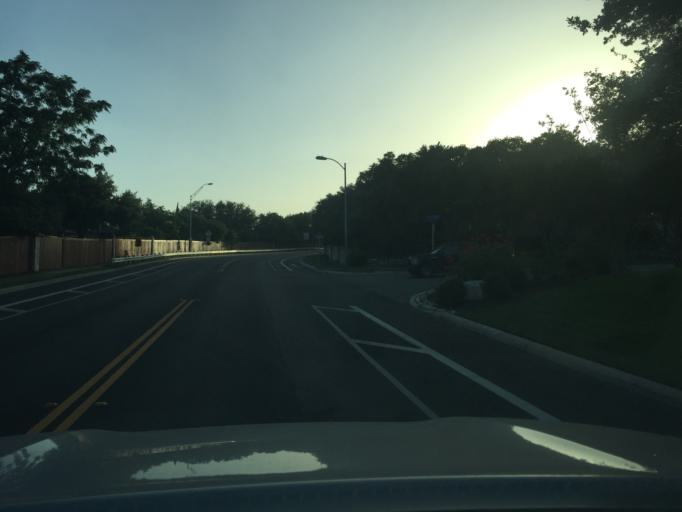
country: US
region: Texas
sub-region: Bexar County
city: Hollywood Park
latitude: 29.6321
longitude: -98.4913
